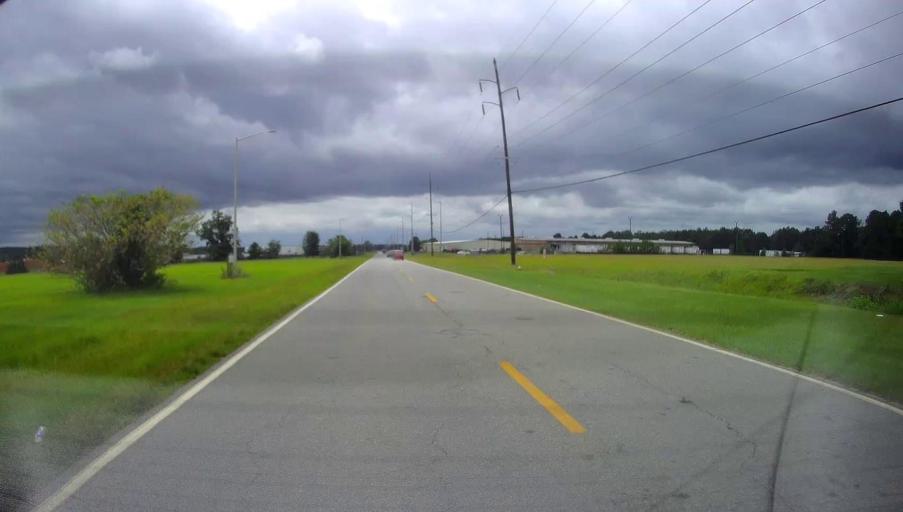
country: US
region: Georgia
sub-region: Bibb County
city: Macon
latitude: 32.8088
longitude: -83.5459
